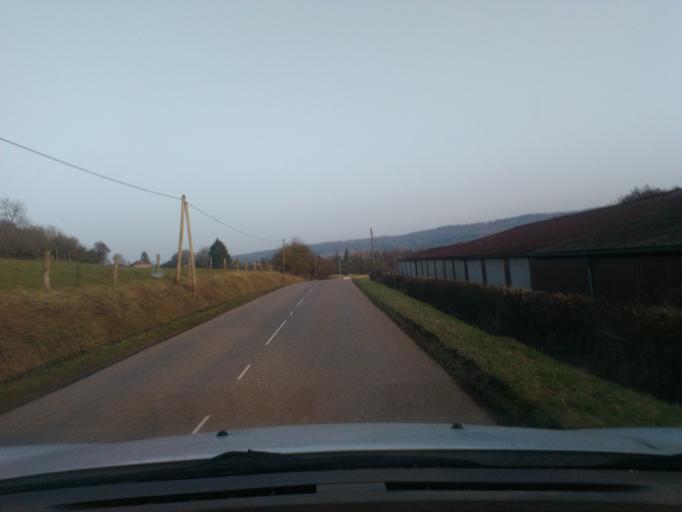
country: FR
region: Lorraine
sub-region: Departement des Vosges
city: Mirecourt
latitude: 48.2778
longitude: 6.0323
